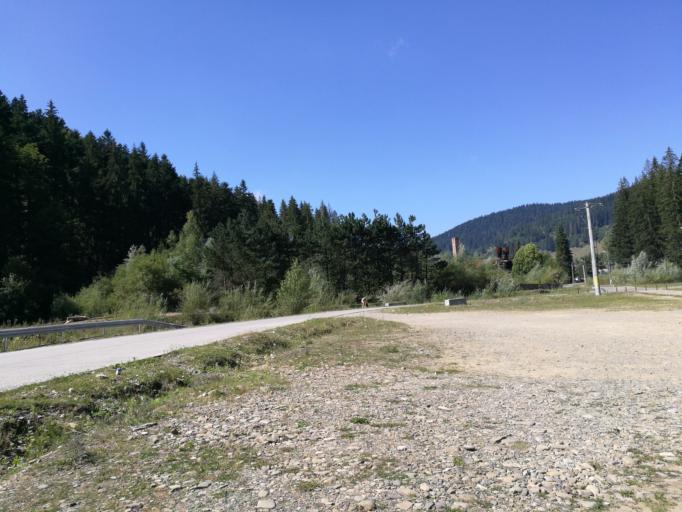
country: RO
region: Suceava
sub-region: Comuna Putna
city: Putna
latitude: 47.8648
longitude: 25.6181
